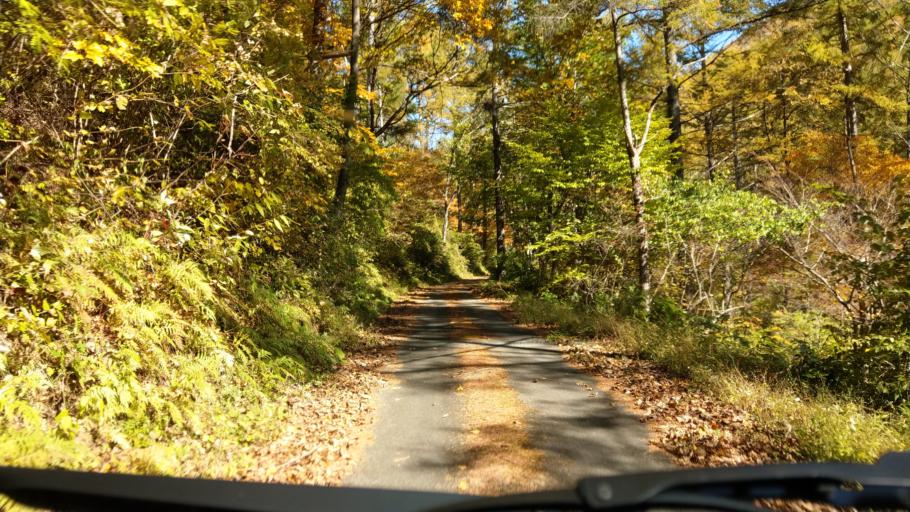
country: JP
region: Nagano
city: Komoro
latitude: 36.3835
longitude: 138.4354
